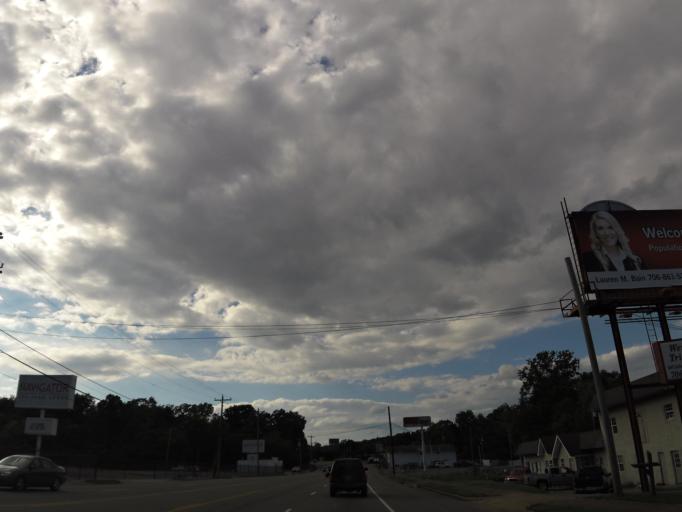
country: US
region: Georgia
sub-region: Catoosa County
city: Lakeview
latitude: 34.9643
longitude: -85.2604
